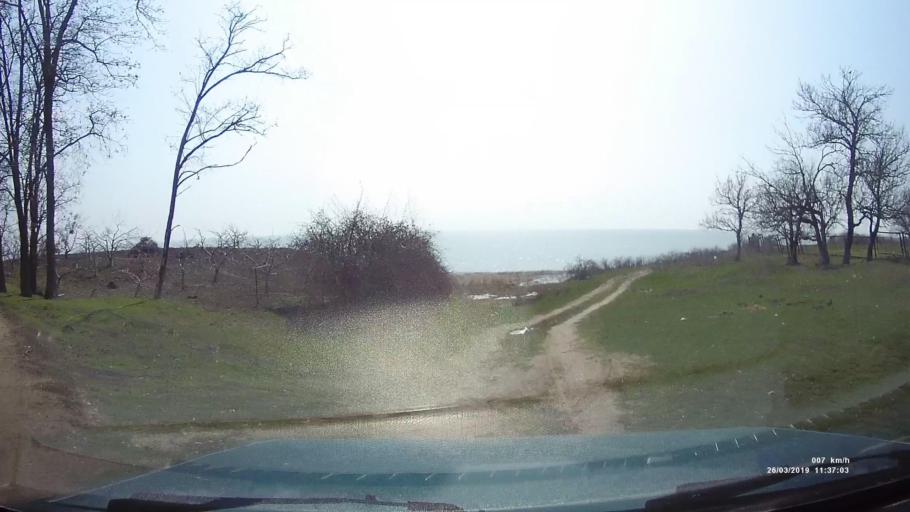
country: RU
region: Rostov
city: Novobessergenovka
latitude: 47.1456
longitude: 38.6427
